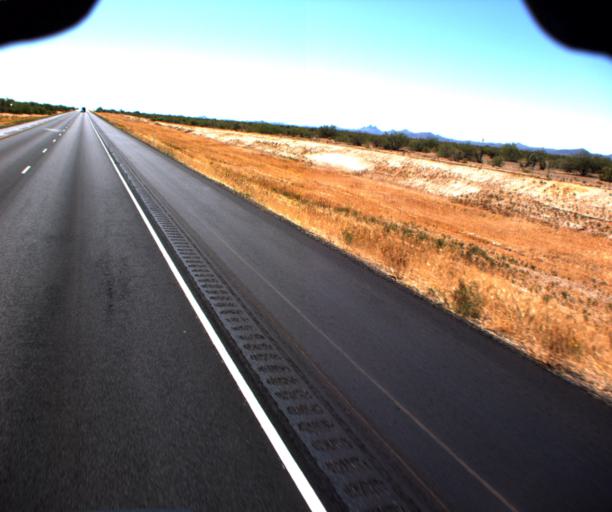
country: US
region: Arizona
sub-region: Yavapai County
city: Congress
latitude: 34.0963
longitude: -112.9122
